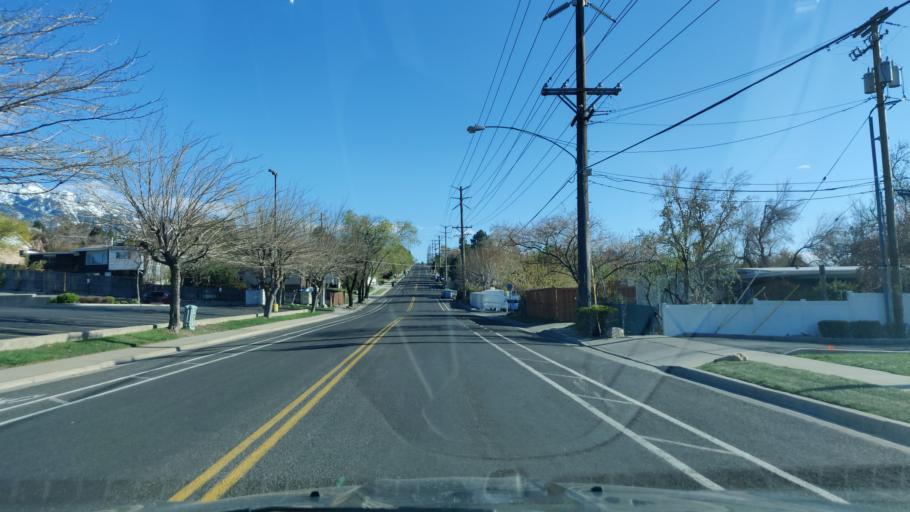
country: US
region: Utah
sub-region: Salt Lake County
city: Cottonwood Heights
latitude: 40.6224
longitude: -111.8248
